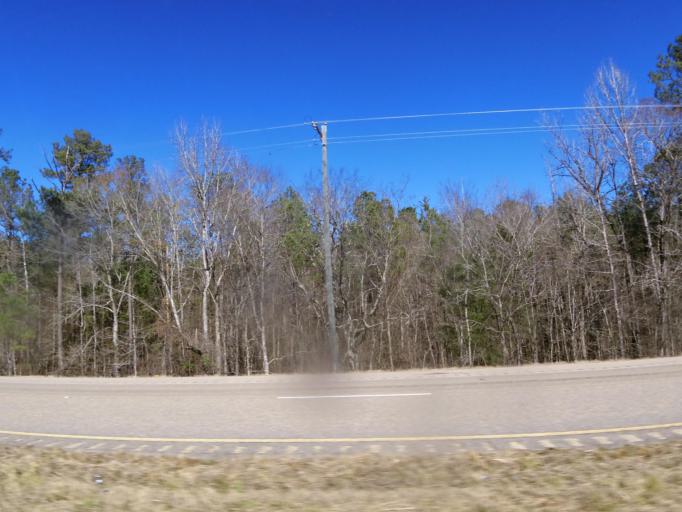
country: US
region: Alabama
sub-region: Montgomery County
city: Pike Road
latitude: 32.1912
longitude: -86.1143
